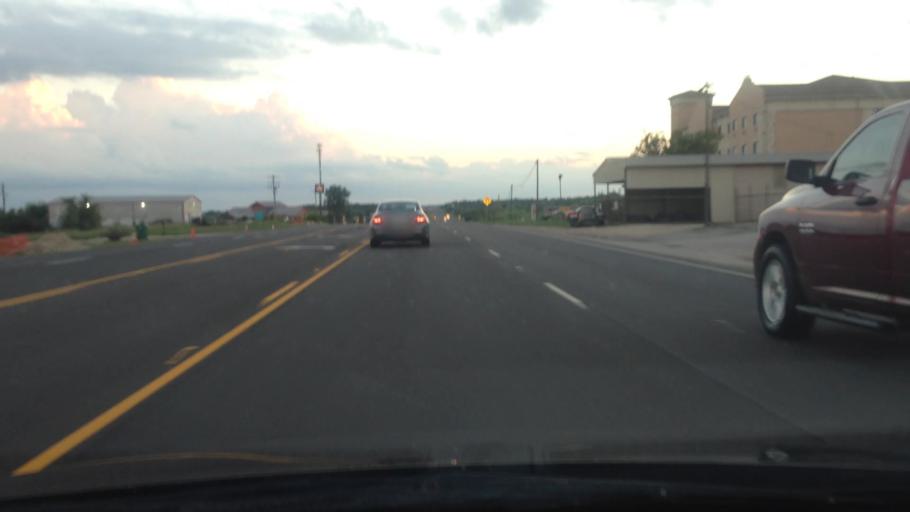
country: US
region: Texas
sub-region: Hood County
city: DeCordova
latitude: 32.5286
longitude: -97.6212
